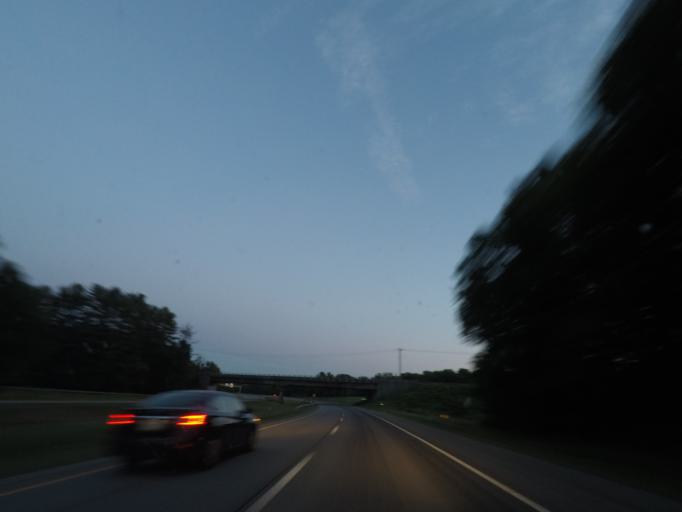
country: US
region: Connecticut
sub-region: Windham County
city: Putnam
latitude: 41.9007
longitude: -71.8991
